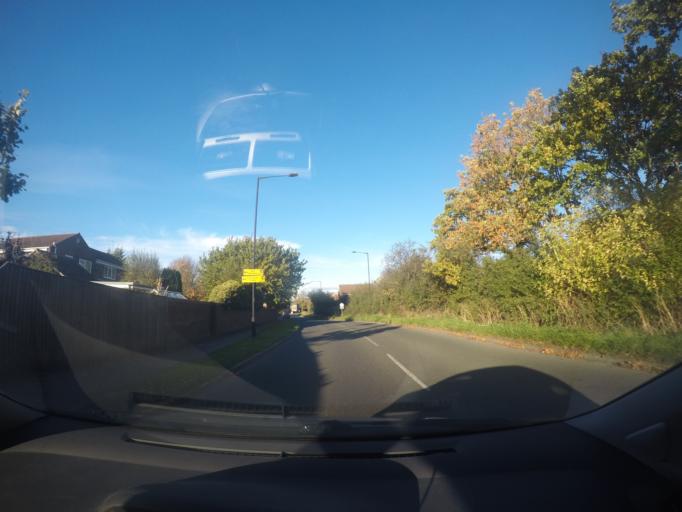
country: GB
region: England
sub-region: City of York
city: York
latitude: 53.9798
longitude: -1.0955
